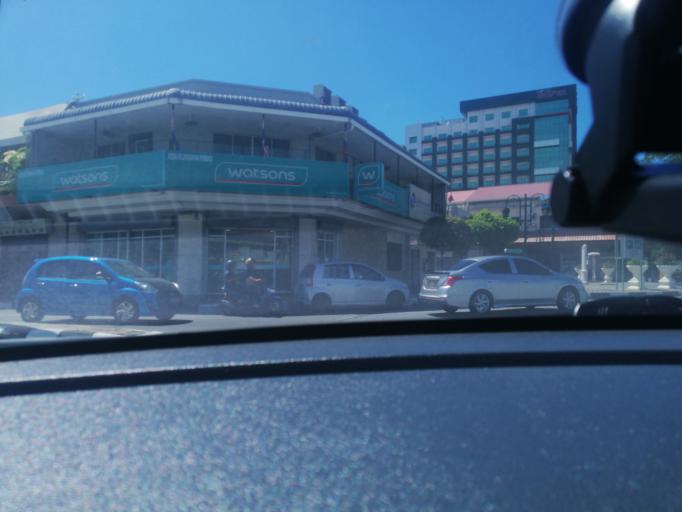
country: MY
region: Labuan
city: Victoria
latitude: 5.2770
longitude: 115.2432
